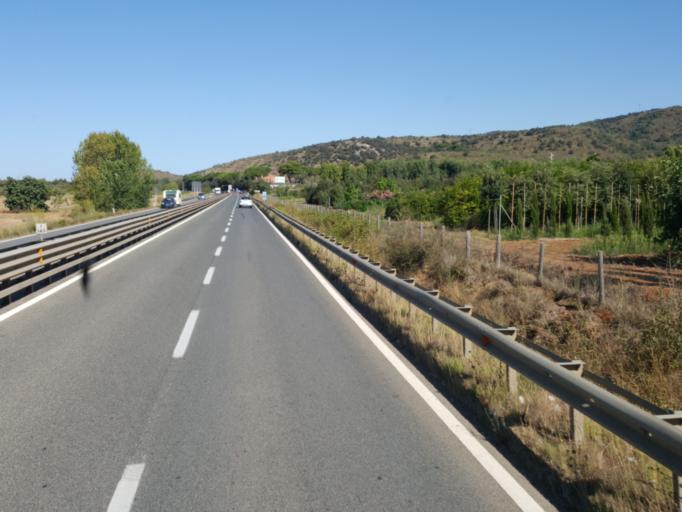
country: IT
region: Tuscany
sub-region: Provincia di Grosseto
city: Orbetello Scalo
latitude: 42.4333
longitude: 11.2825
